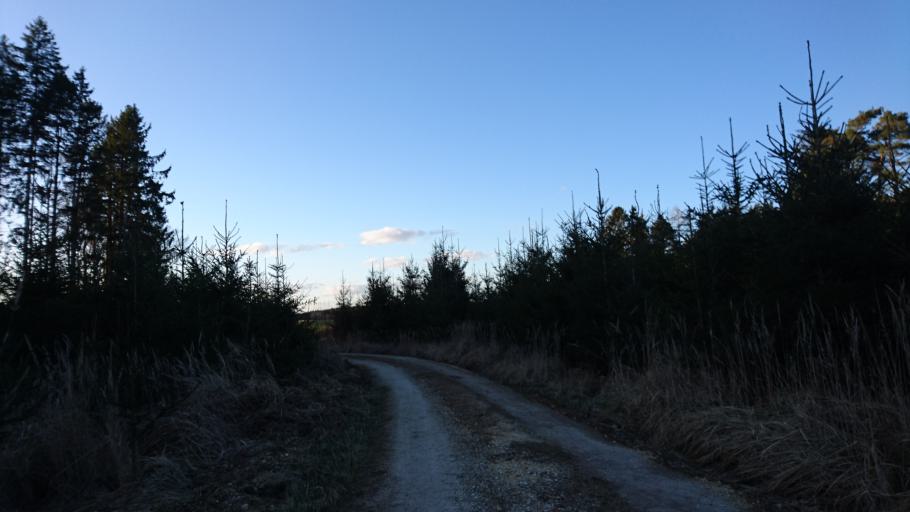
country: DE
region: Bavaria
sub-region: Swabia
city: Altenmunster
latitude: 48.4369
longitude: 10.6208
